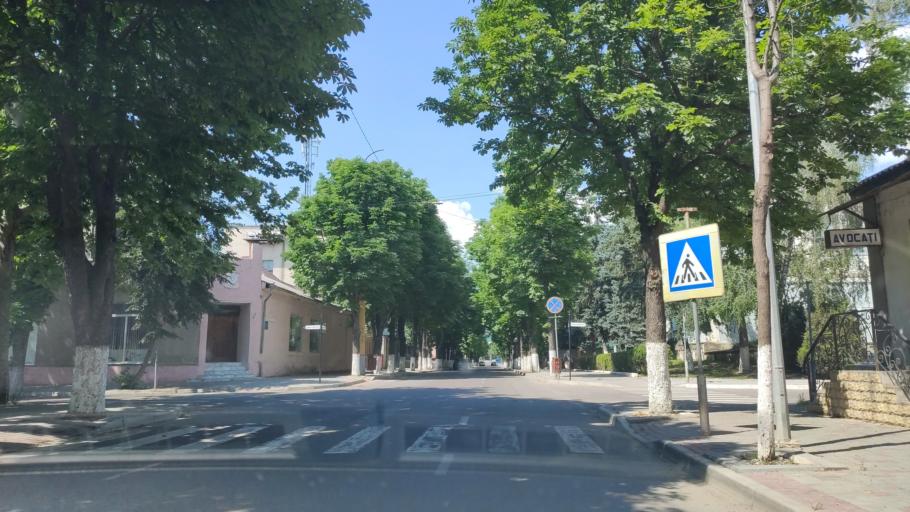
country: MD
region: Raionul Soroca
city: Soroca
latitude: 48.1538
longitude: 28.3021
